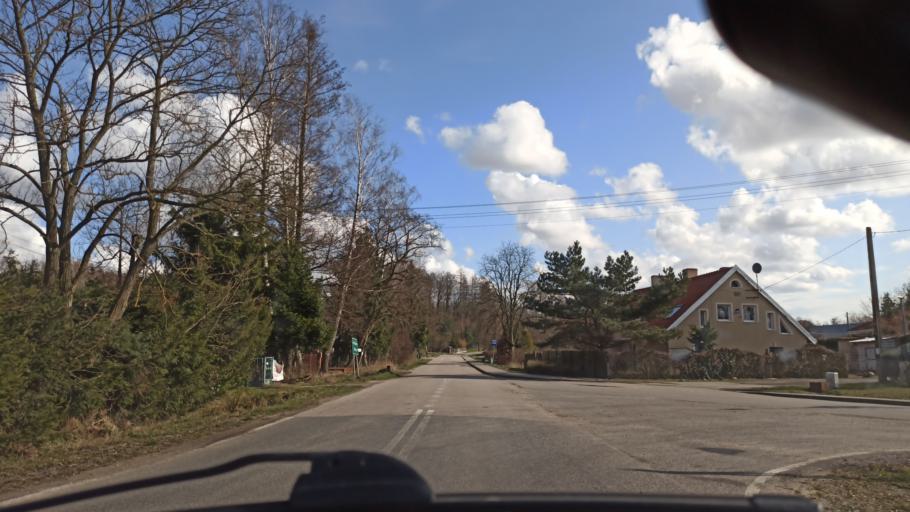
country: PL
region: Warmian-Masurian Voivodeship
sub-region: Powiat elblaski
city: Tolkmicko
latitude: 54.2685
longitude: 19.4749
